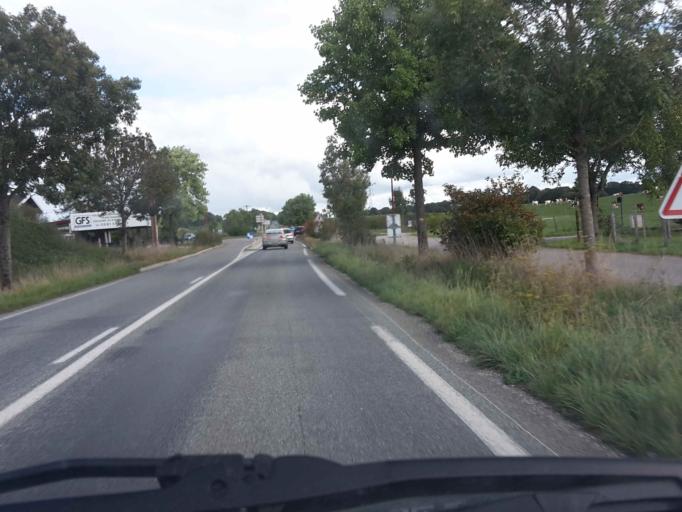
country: FR
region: Franche-Comte
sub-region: Departement du Doubs
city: Saone
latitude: 47.2400
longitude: 6.1214
